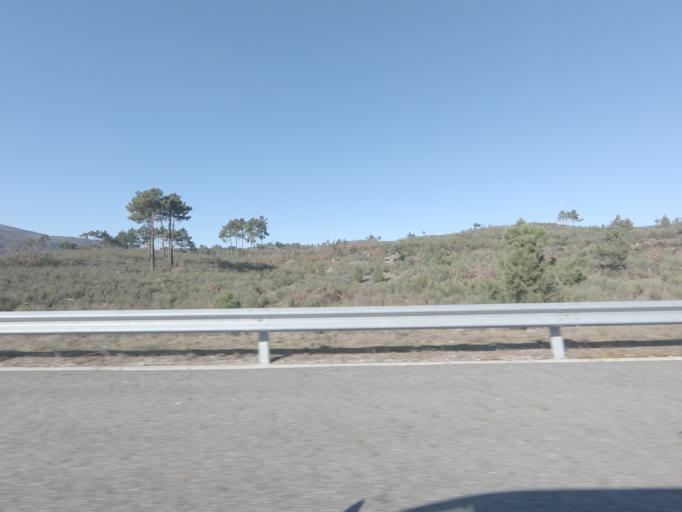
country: PT
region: Vila Real
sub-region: Chaves
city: Chaves
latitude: 41.7863
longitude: -7.4621
